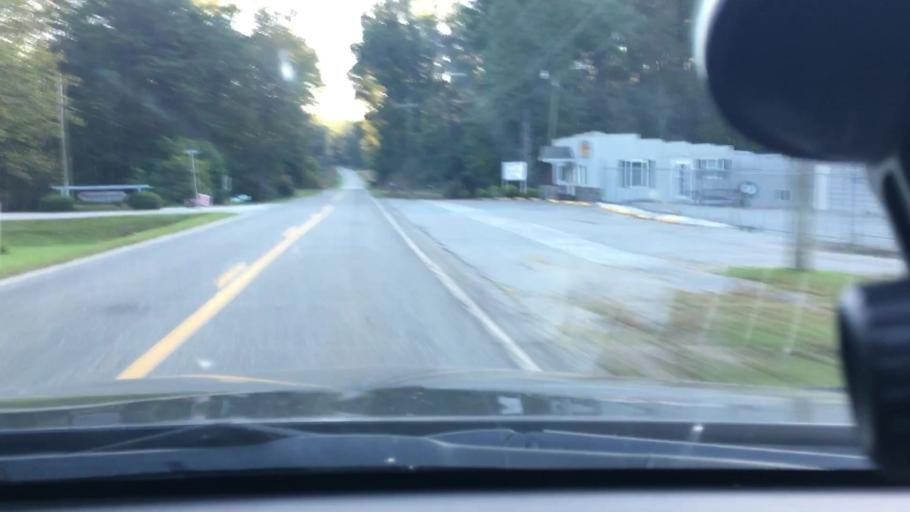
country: US
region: North Carolina
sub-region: Polk County
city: Columbus
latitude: 35.2782
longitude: -82.1802
